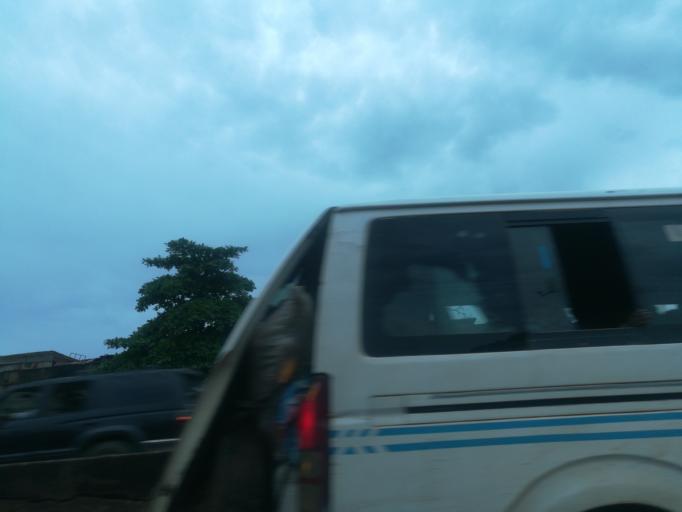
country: NG
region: Oyo
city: Ibadan
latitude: 7.3942
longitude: 3.9574
